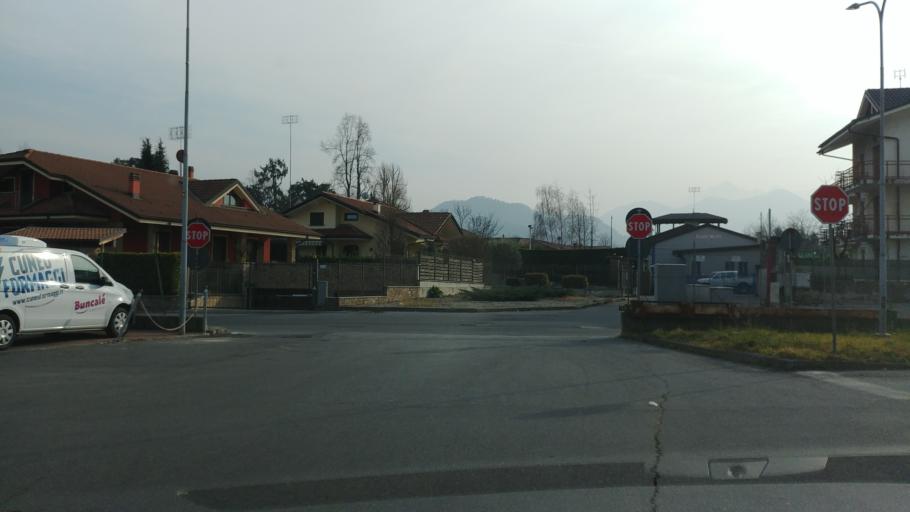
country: IT
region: Piedmont
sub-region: Provincia di Cuneo
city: Borgo San Dalmazzo
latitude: 44.3469
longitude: 7.5082
